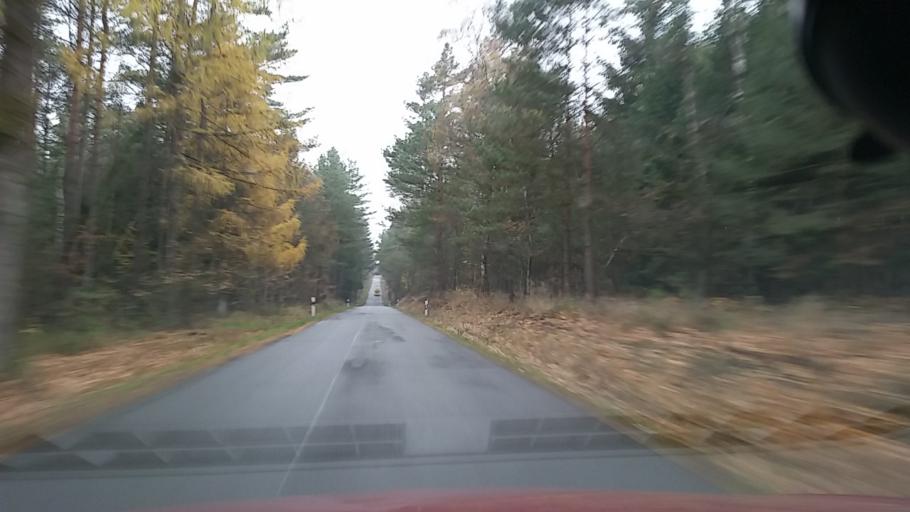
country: DE
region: Lower Saxony
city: Obernholz
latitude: 52.7819
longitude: 10.5766
